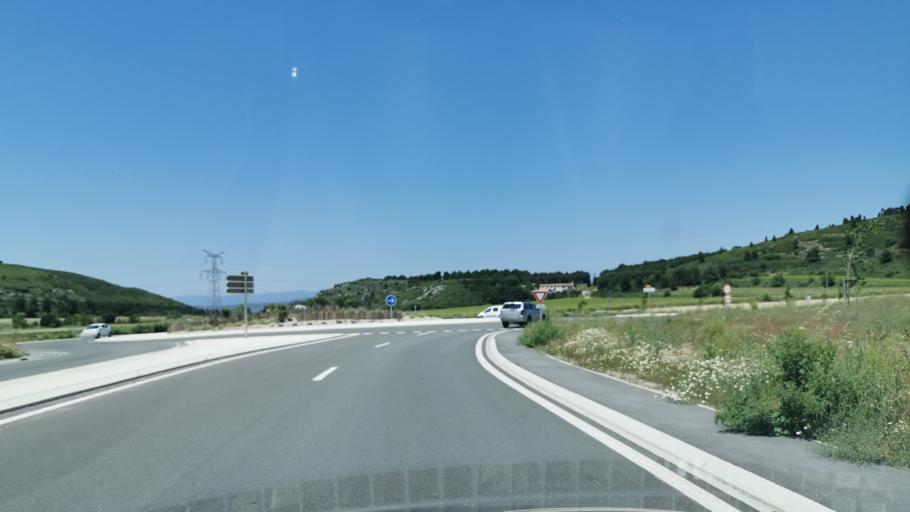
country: FR
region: Languedoc-Roussillon
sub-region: Departement de l'Aude
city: Nevian
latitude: 43.1973
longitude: 2.8997
